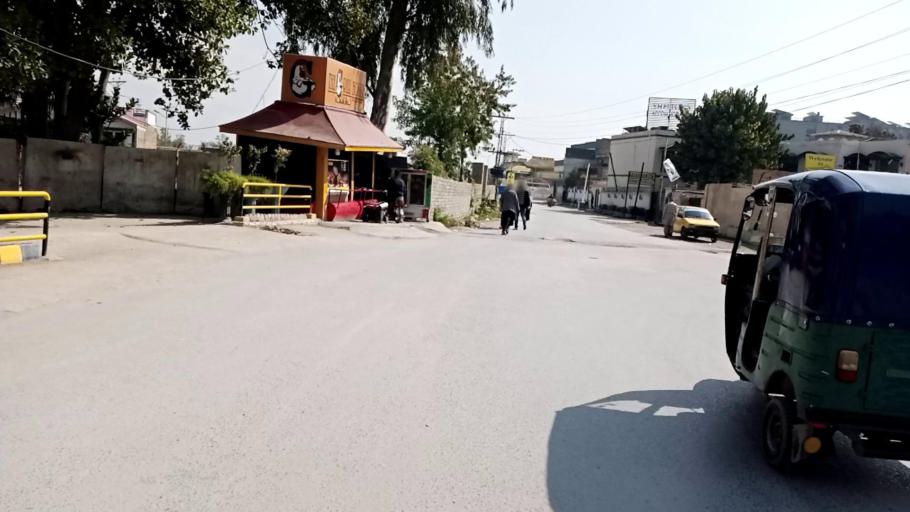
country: PK
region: Khyber Pakhtunkhwa
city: Peshawar
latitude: 33.9977
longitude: 71.5008
